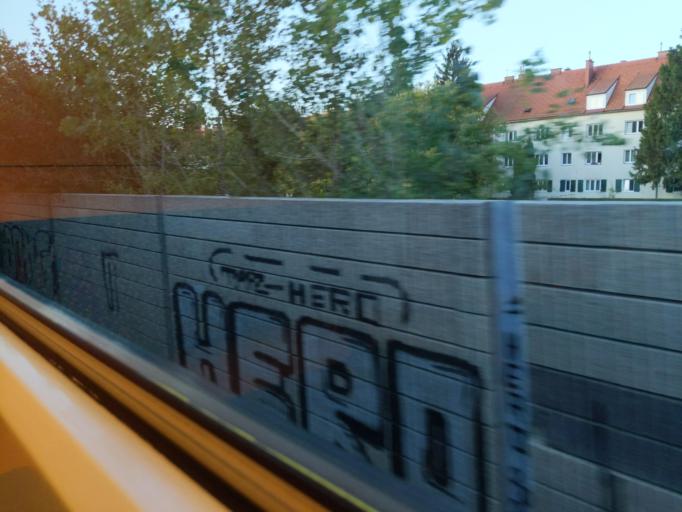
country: AT
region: Lower Austria
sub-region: Politischer Bezirk Korneuburg
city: Langenzersdorf
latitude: 48.2866
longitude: 16.3806
